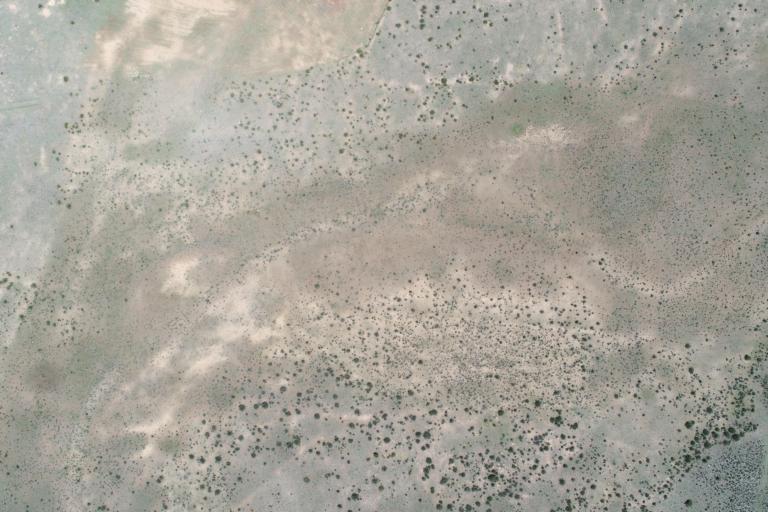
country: BO
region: La Paz
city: Curahuara de Carangas
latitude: -17.2811
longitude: -68.5172
